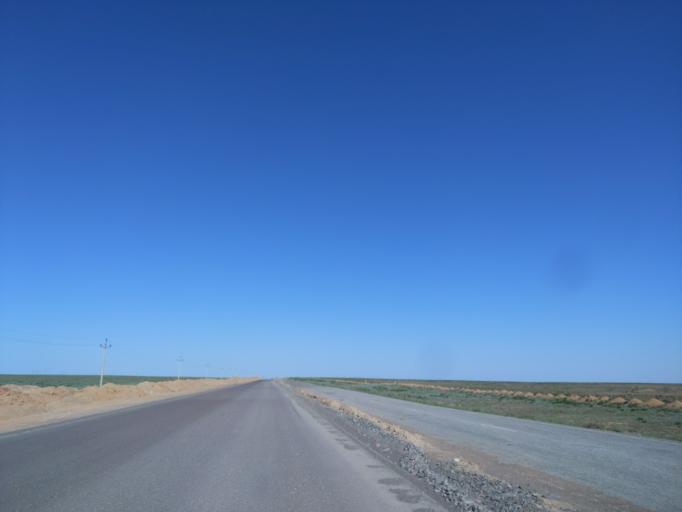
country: KZ
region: Almaty Oblysy
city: Bakanas
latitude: 44.1599
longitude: 75.8430
